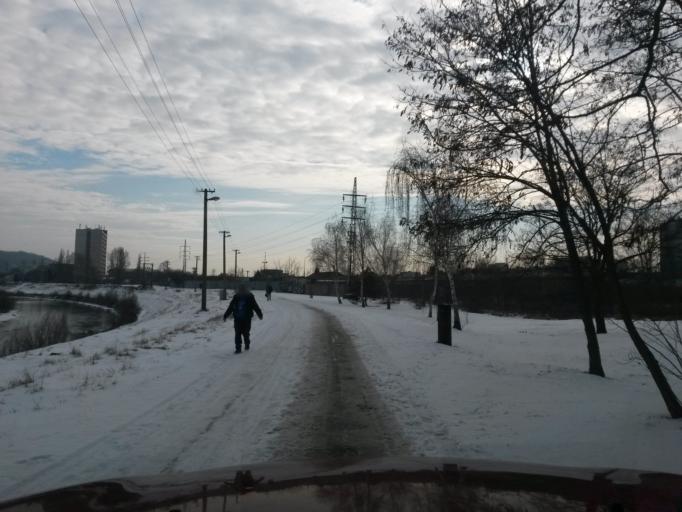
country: SK
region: Kosicky
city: Kosice
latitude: 48.7262
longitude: 21.2702
